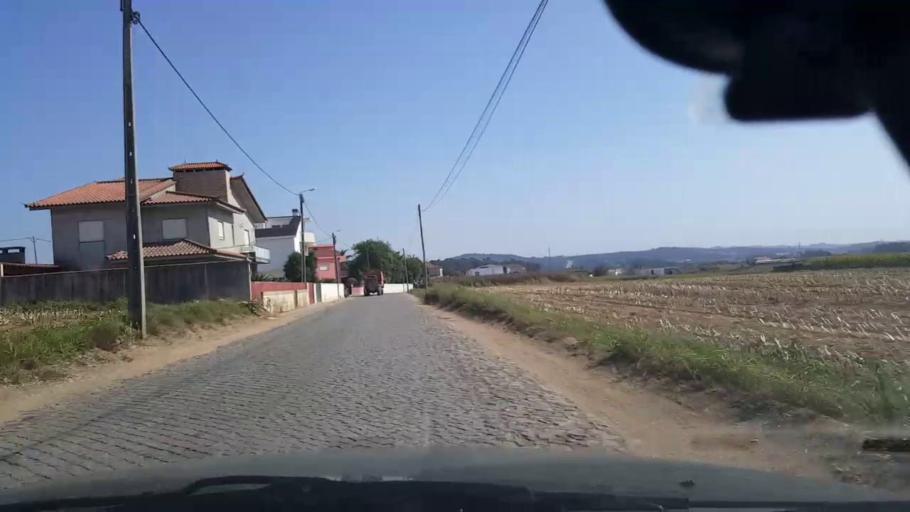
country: PT
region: Porto
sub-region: Povoa de Varzim
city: Pedroso
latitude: 41.4123
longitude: -8.6978
